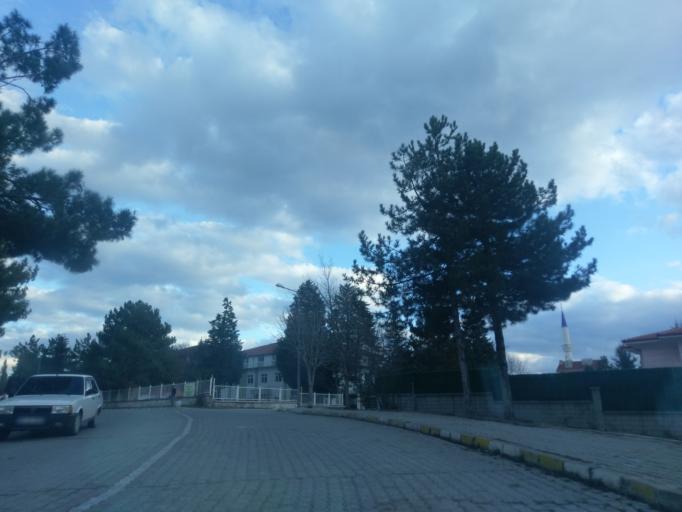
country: TR
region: Kuetahya
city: Gediz
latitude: 38.9877
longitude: 29.3903
